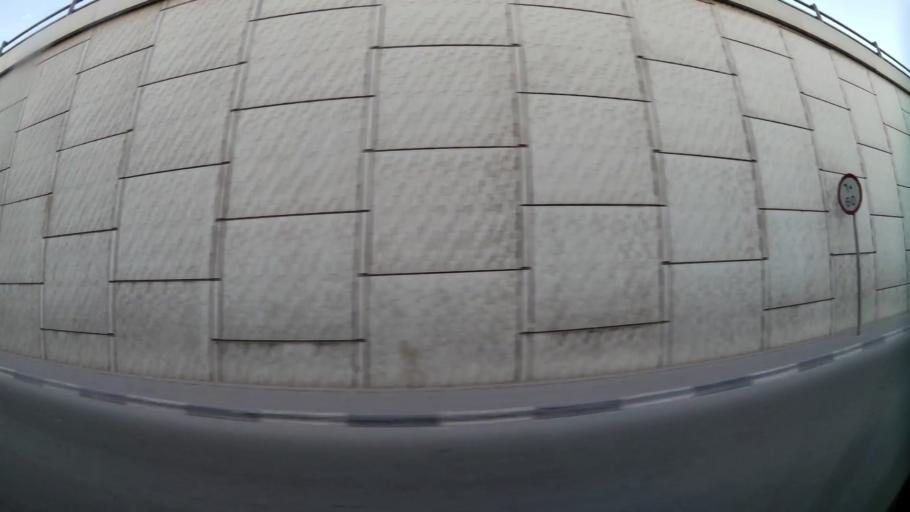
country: QA
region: Baladiyat ar Rayyan
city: Ar Rayyan
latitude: 25.3195
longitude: 51.4700
